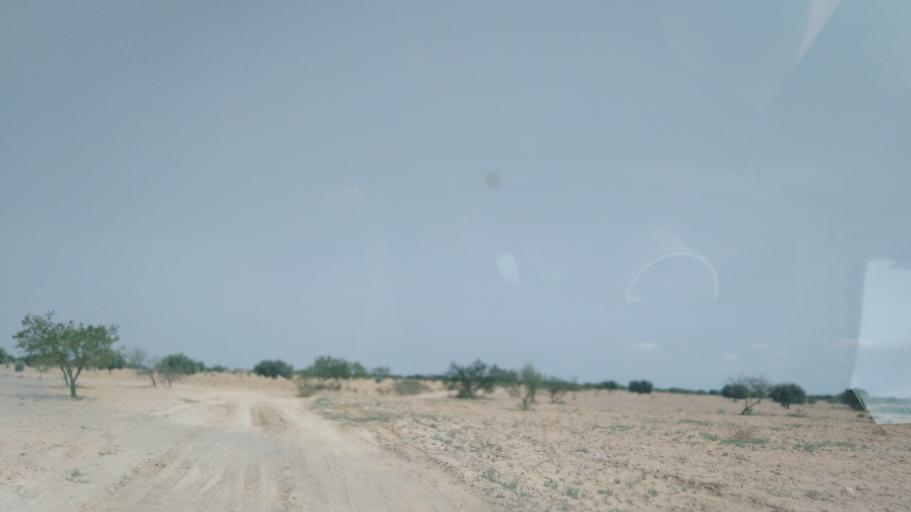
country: TN
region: Safaqis
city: Sfax
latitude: 34.6463
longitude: 10.5584
